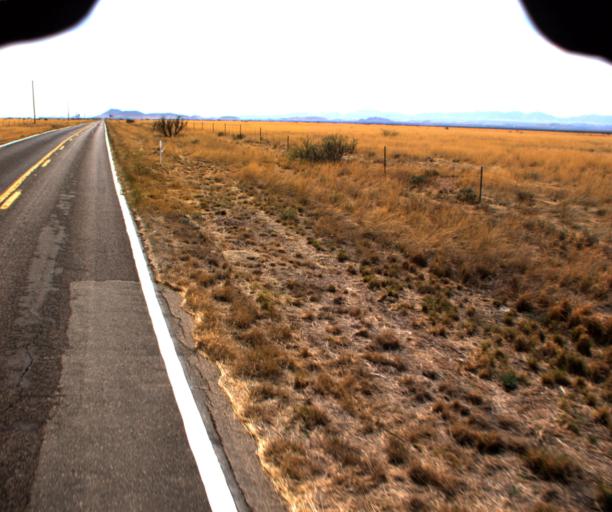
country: US
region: Arizona
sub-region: Cochise County
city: Willcox
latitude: 31.9486
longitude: -109.4790
